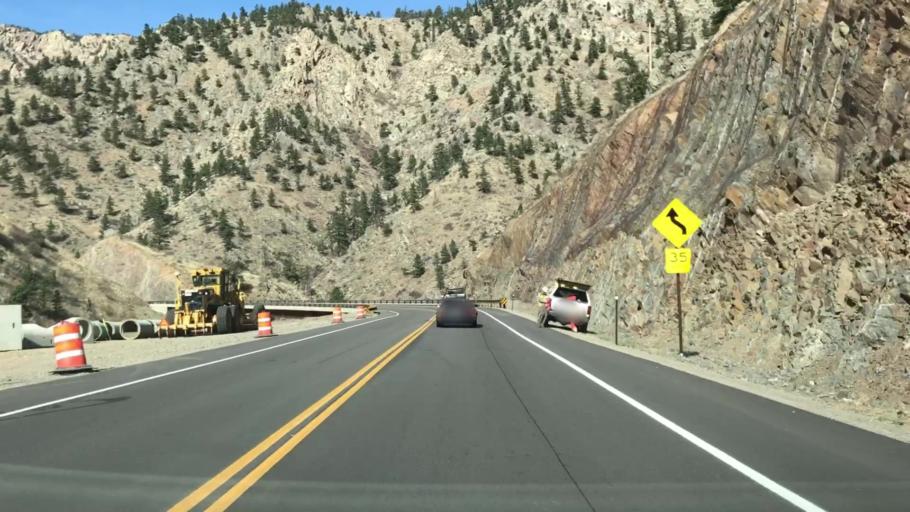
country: US
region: Colorado
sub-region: Boulder County
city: Lyons
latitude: 40.4252
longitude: -105.2929
